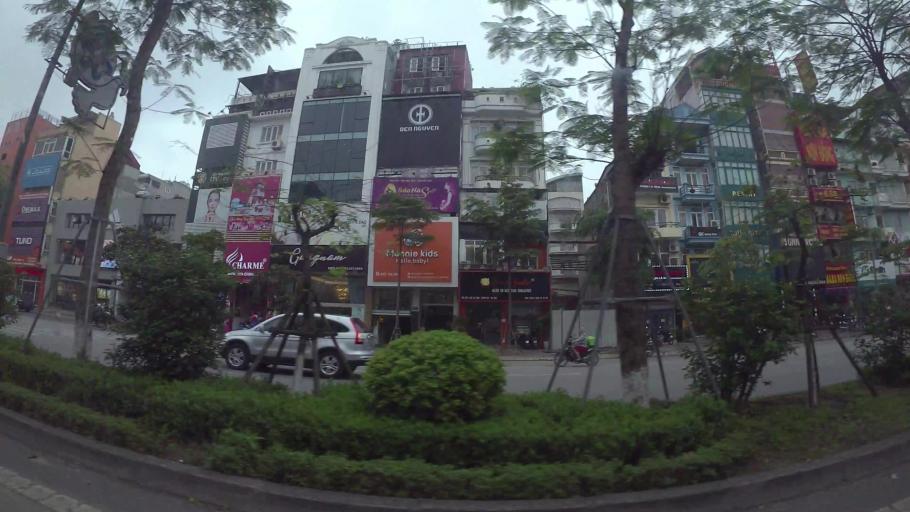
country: VN
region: Ha Noi
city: Dong Da
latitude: 21.0160
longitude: 105.8324
